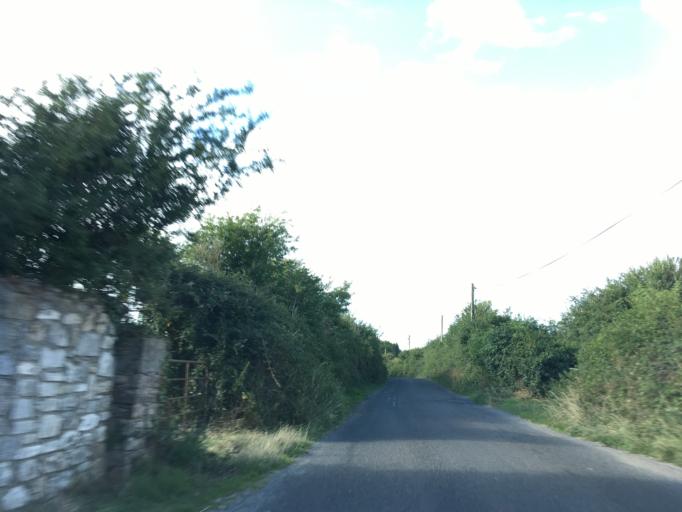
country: IE
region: Munster
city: Cahir
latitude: 52.2724
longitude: -7.9563
